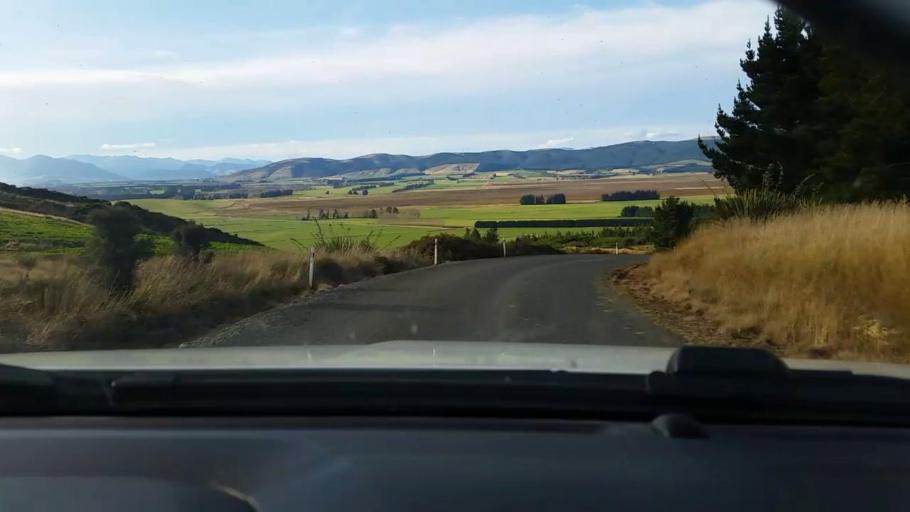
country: NZ
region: Southland
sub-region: Southland District
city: Winton
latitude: -45.8190
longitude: 168.1744
